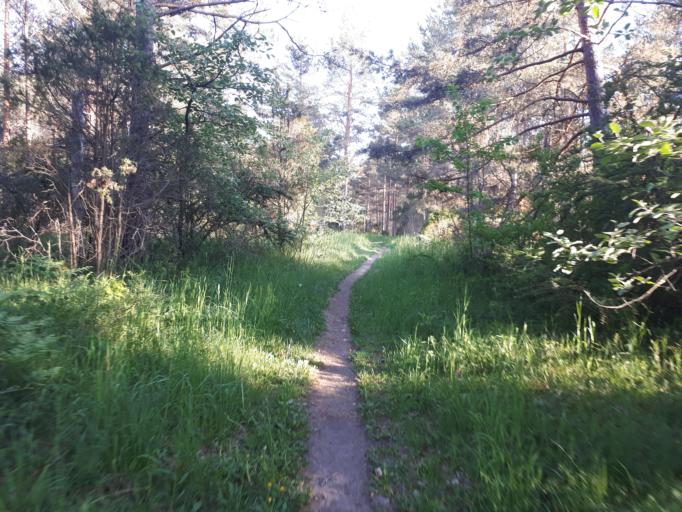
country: SE
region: Gotland
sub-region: Gotland
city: Visby
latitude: 57.6054
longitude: 18.2978
